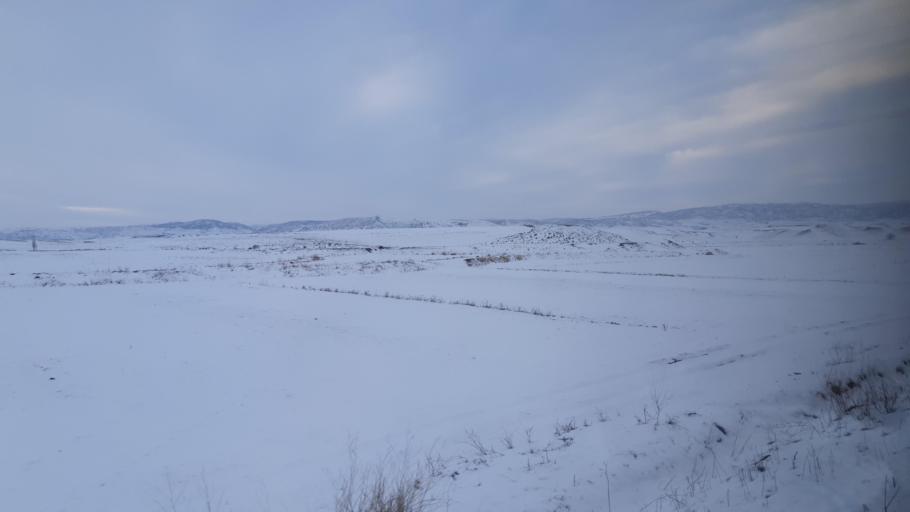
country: TR
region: Yozgat
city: Yerkoy
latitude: 39.6873
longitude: 34.4092
